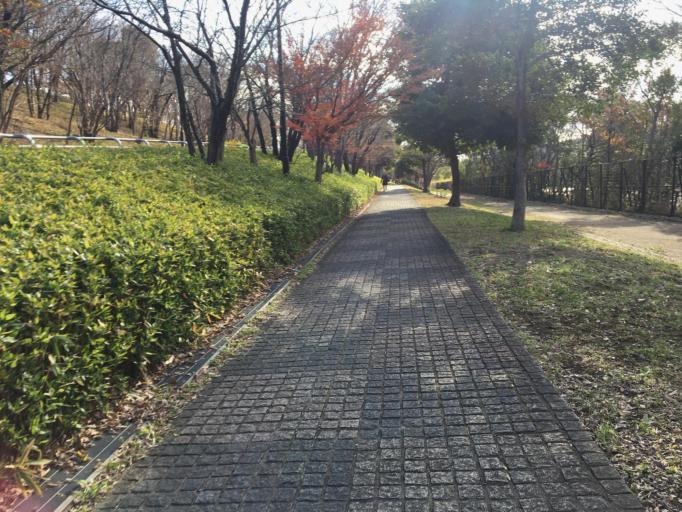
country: JP
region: Tokyo
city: Urayasu
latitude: 35.6874
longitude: 139.8479
